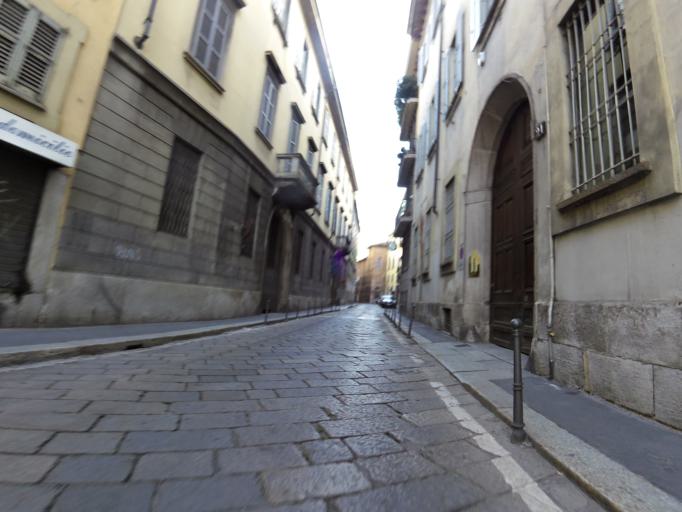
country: IT
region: Lombardy
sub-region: Citta metropolitana di Milano
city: Milano
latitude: 45.4638
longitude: 9.1794
